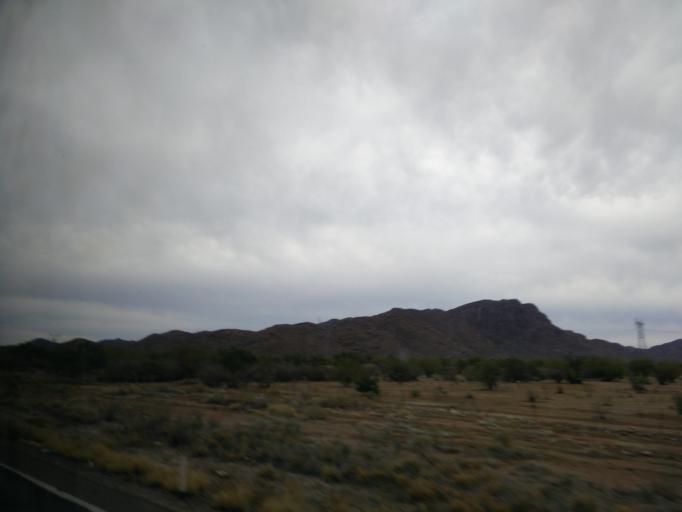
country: MX
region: Sonora
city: Hermosillo
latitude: 28.5954
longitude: -111.0233
